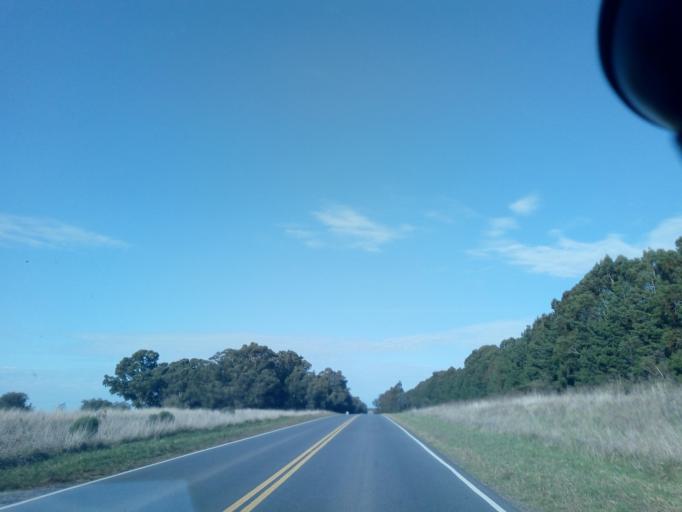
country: AR
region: Buenos Aires
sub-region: Partido de Tandil
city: Tandil
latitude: -37.3524
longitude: -58.8847
